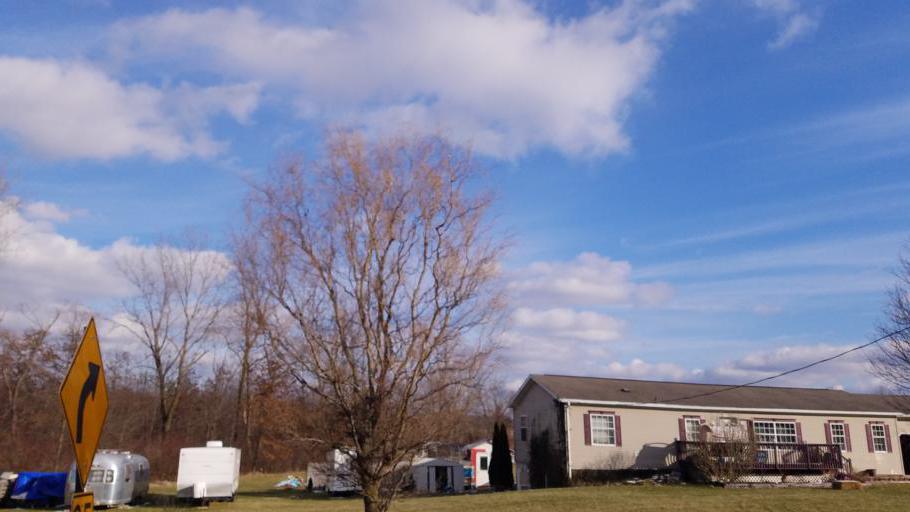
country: US
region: Ohio
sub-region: Crawford County
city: Crestline
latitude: 40.7752
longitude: -82.6789
